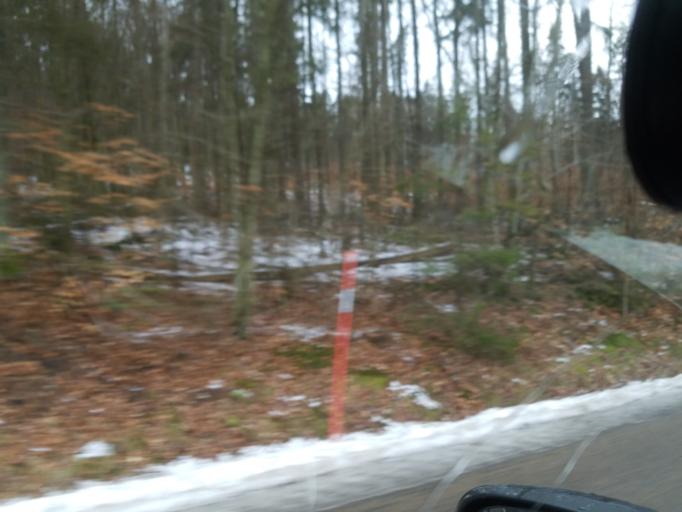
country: SE
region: Vaestra Goetaland
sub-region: Orust
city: Henan
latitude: 58.3019
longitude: 11.6616
